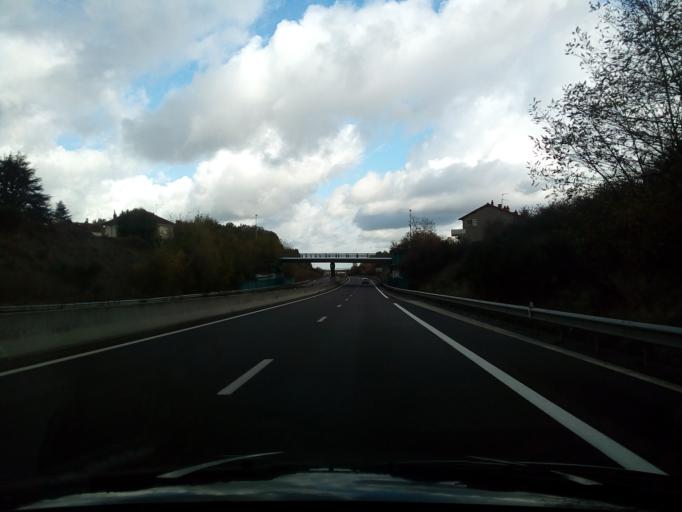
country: FR
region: Auvergne
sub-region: Departement de l'Allier
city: Domerat
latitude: 46.3480
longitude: 2.5422
